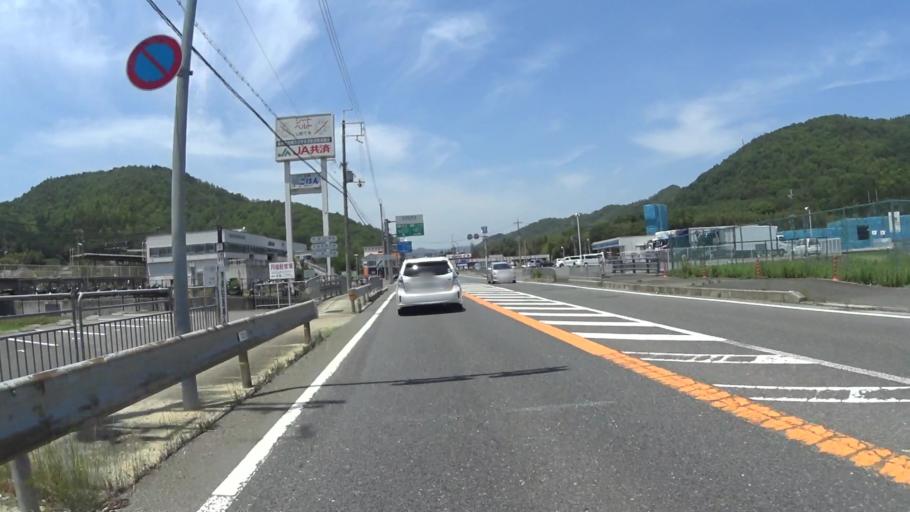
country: JP
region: Kyoto
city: Kameoka
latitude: 35.0917
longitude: 135.4995
